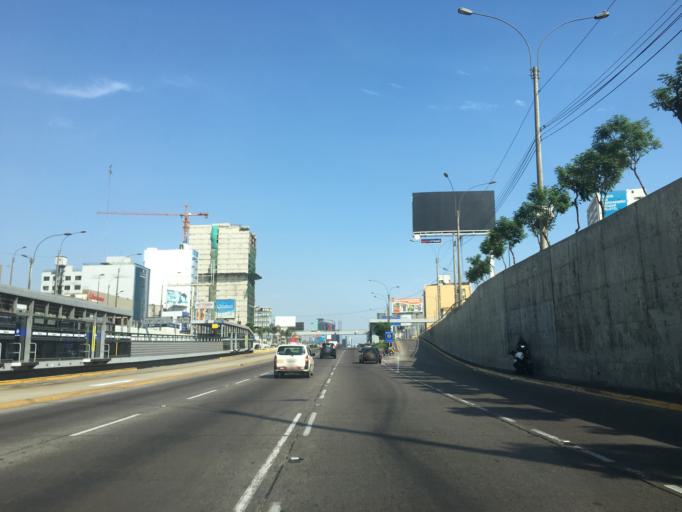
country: PE
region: Lima
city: Lima
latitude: -12.0773
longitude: -77.0289
